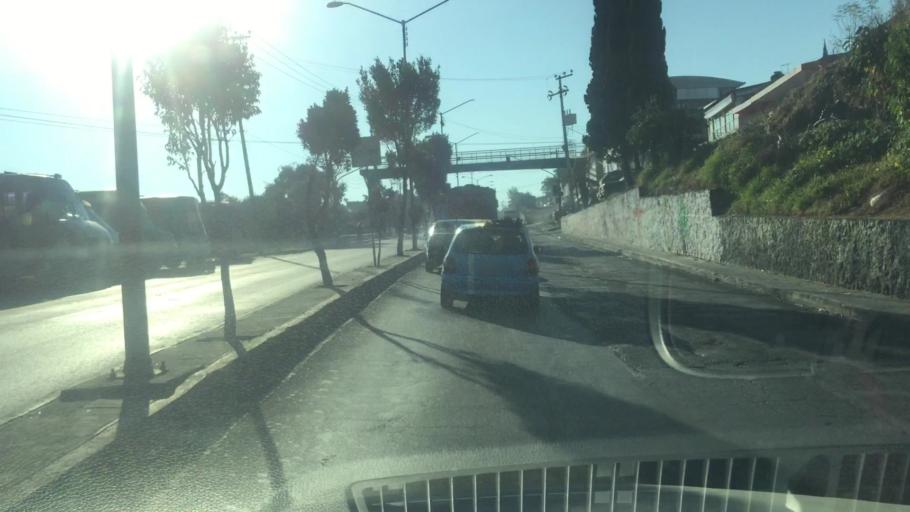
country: MX
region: Mexico City
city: Tlalpan
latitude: 19.2781
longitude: -99.2100
